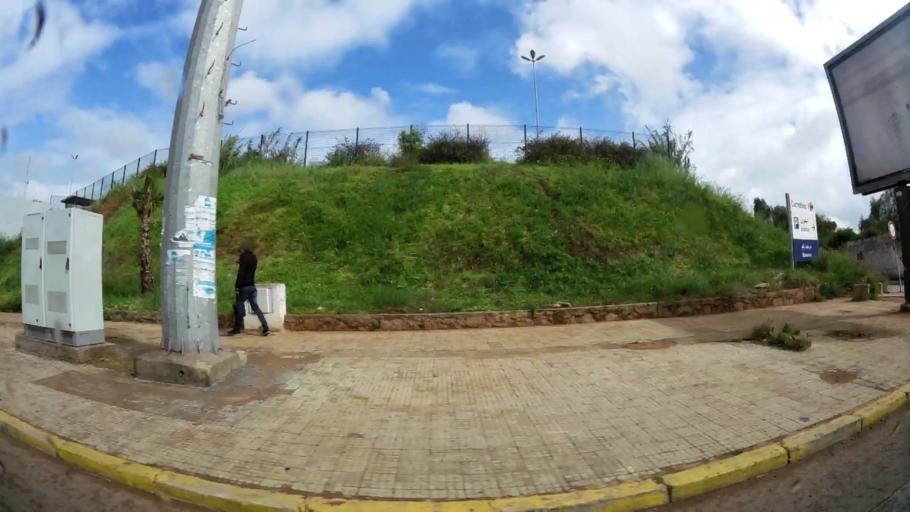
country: MA
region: Grand Casablanca
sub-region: Casablanca
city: Casablanca
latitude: 33.5372
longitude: -7.6442
